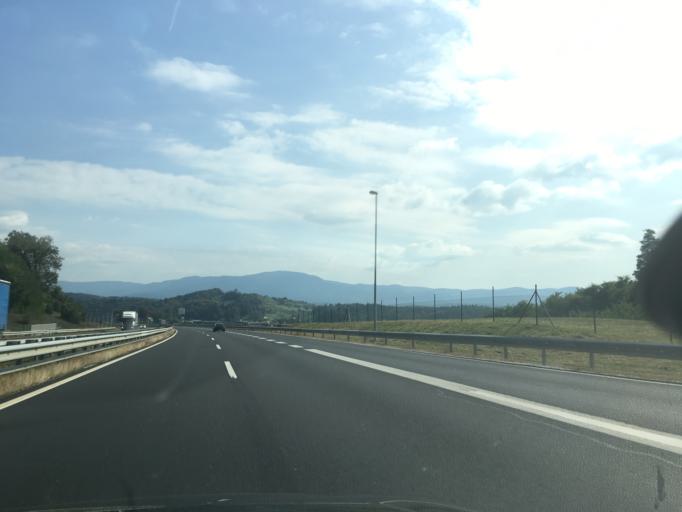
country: SI
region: Novo Mesto
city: Novo Mesto
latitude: 45.8299
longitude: 15.1792
